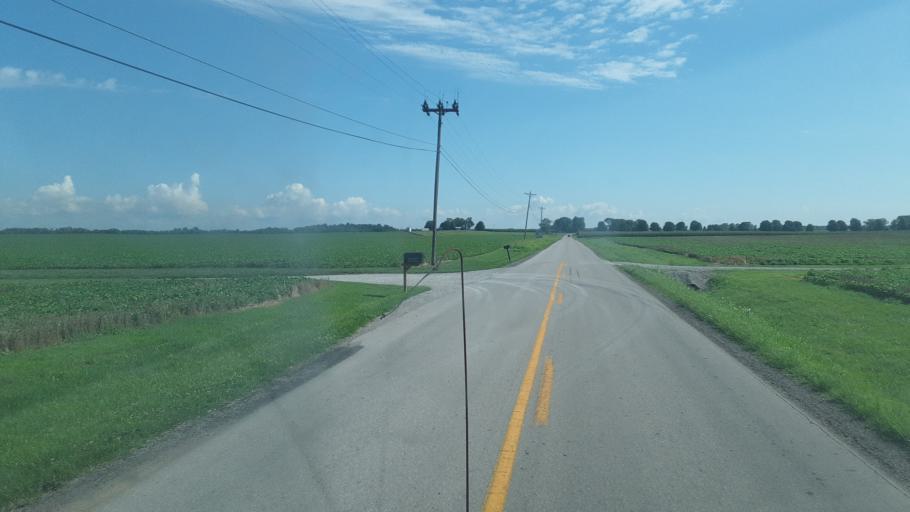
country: US
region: Kentucky
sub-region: Todd County
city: Guthrie
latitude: 36.7262
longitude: -87.2617
